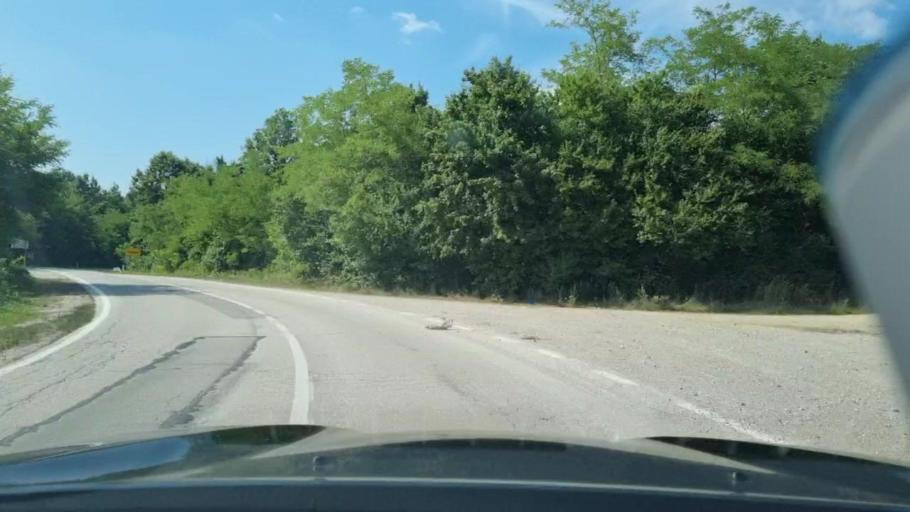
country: BA
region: Federation of Bosnia and Herzegovina
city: Bosanska Krupa
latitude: 44.8422
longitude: 16.1604
